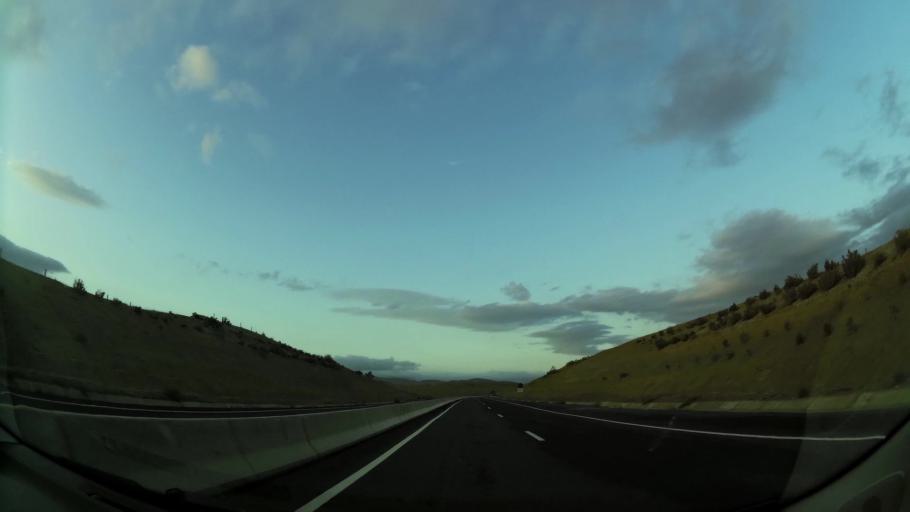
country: MA
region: Oriental
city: Taourirt
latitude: 34.5661
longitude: -2.8315
